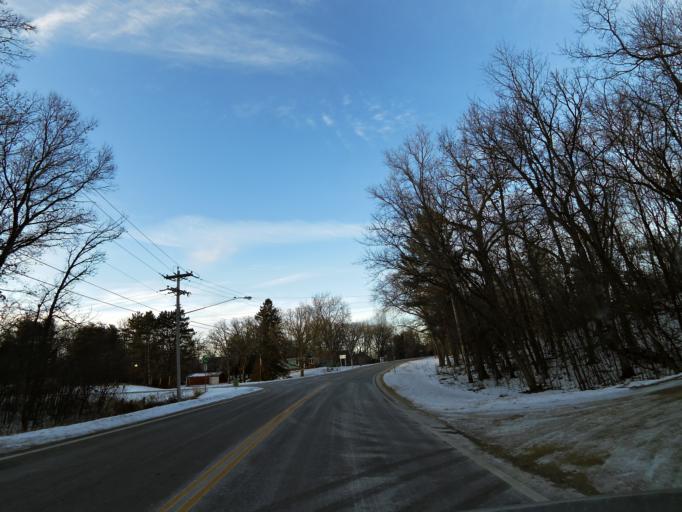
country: US
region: Minnesota
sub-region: Washington County
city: Lake Elmo
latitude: 44.9777
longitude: -92.8641
